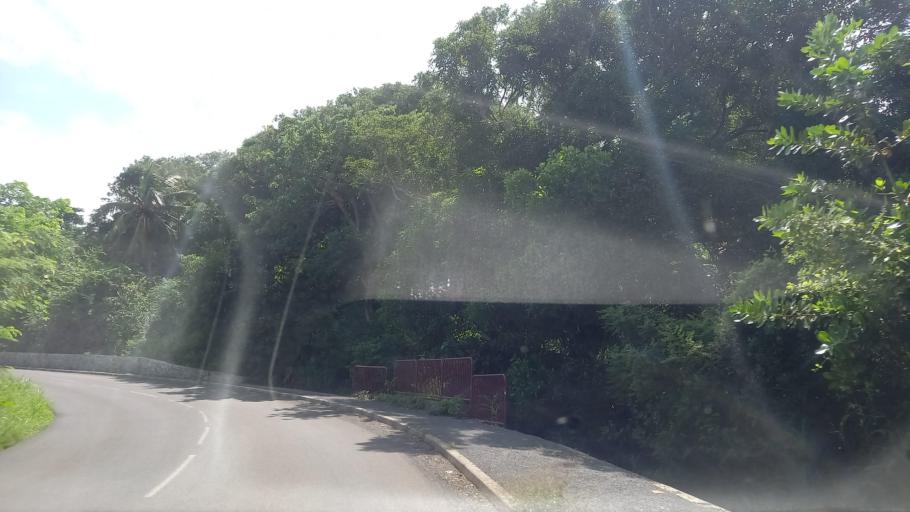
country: YT
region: Boueni
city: Boueni
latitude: -12.9220
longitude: 45.0870
